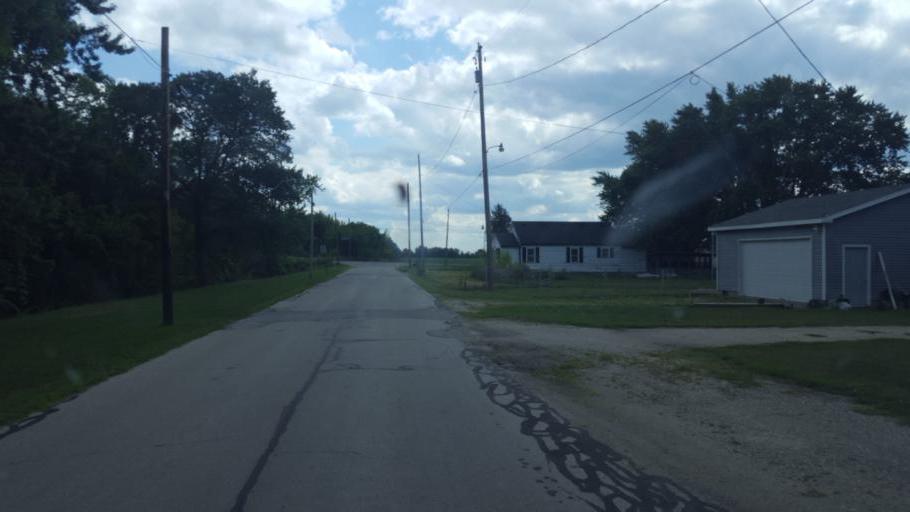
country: US
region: Ohio
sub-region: Lucas County
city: Curtice
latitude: 41.6585
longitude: -83.2538
